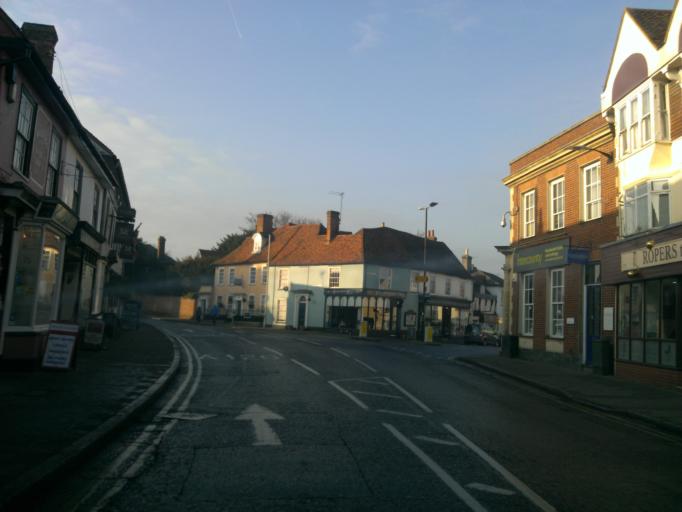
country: GB
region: England
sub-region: Essex
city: Great Dunmow
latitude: 51.8725
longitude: 0.3628
